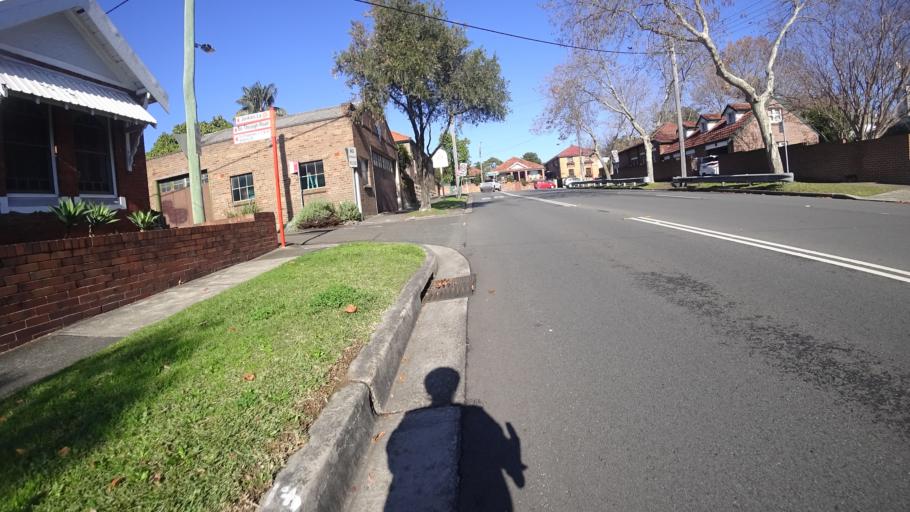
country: AU
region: New South Wales
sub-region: North Sydney
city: Crows Nest
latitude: -33.8220
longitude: 151.2042
